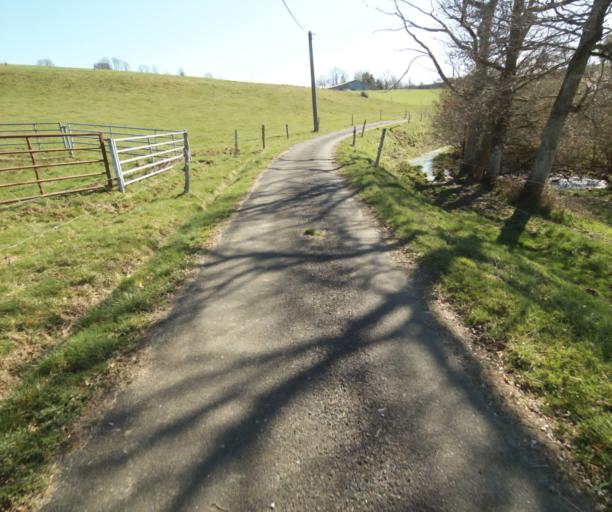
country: FR
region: Limousin
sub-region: Departement de la Correze
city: Chamboulive
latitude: 45.4233
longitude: 1.6677
